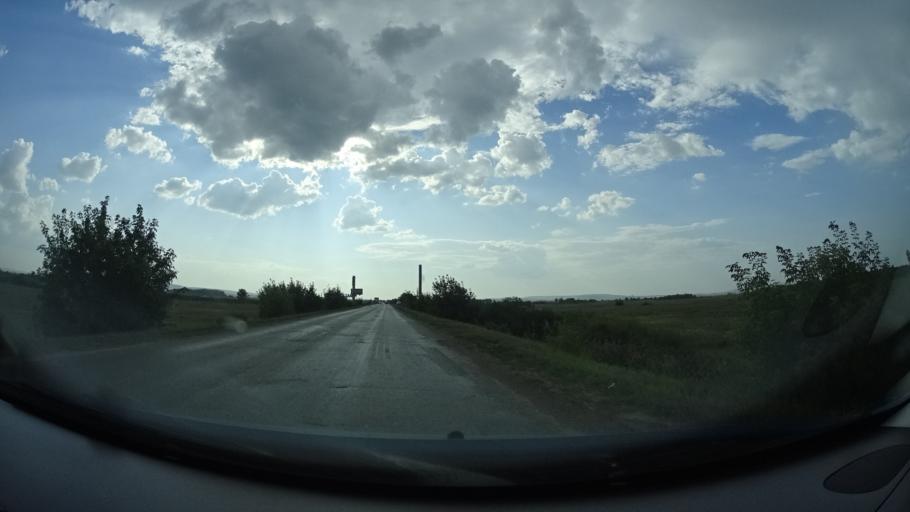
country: RU
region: Bashkortostan
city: Oktyabr'skiy
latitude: 54.4856
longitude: 53.4297
